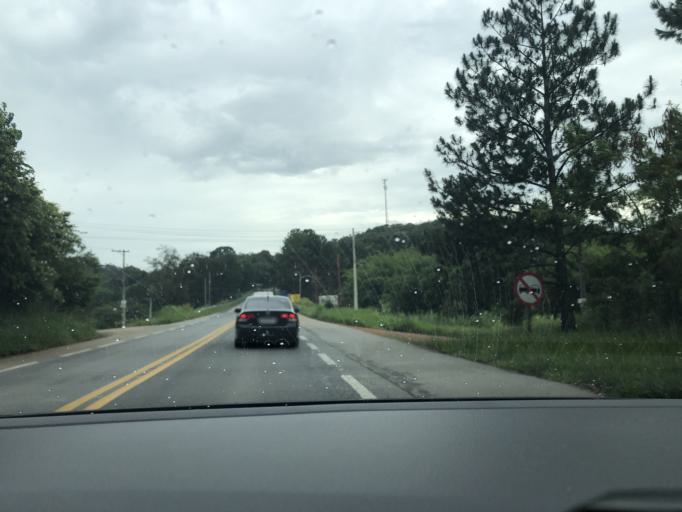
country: BR
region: Sao Paulo
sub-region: Campo Limpo Paulista
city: Campo Limpo Paulista
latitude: -23.1759
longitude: -46.7747
